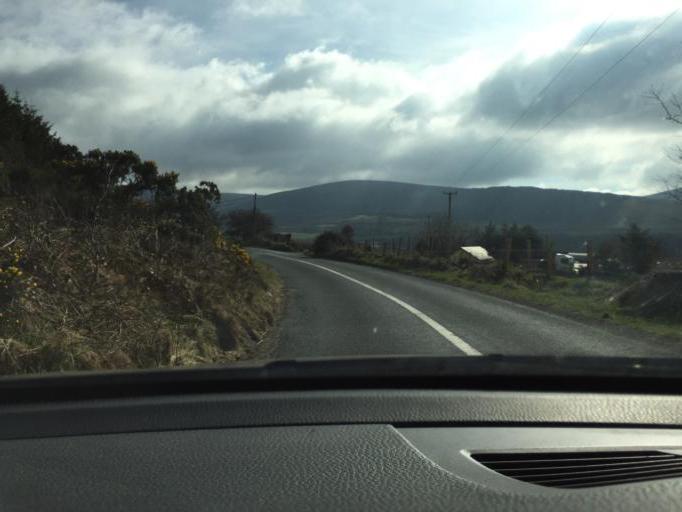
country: IE
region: Leinster
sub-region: Wicklow
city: Valleymount
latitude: 53.0731
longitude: -6.5321
